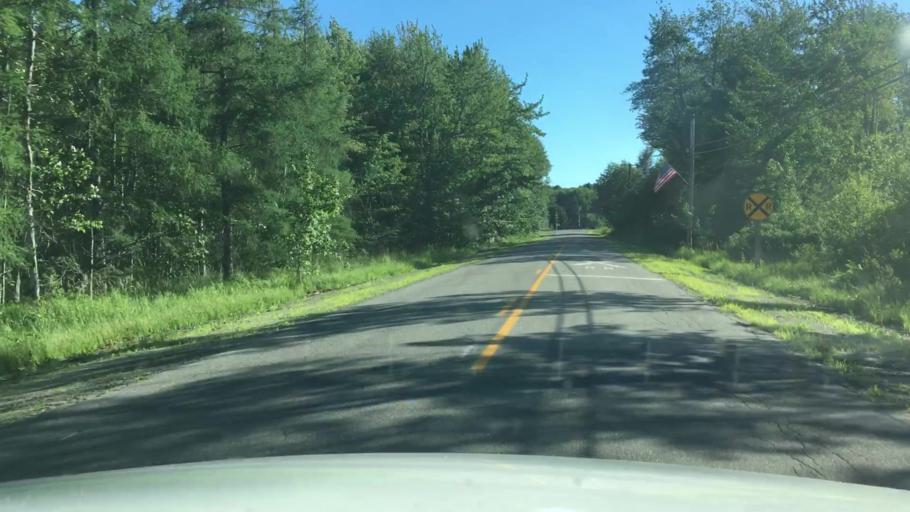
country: US
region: Maine
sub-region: Penobscot County
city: Howland
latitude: 45.1876
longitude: -68.6119
